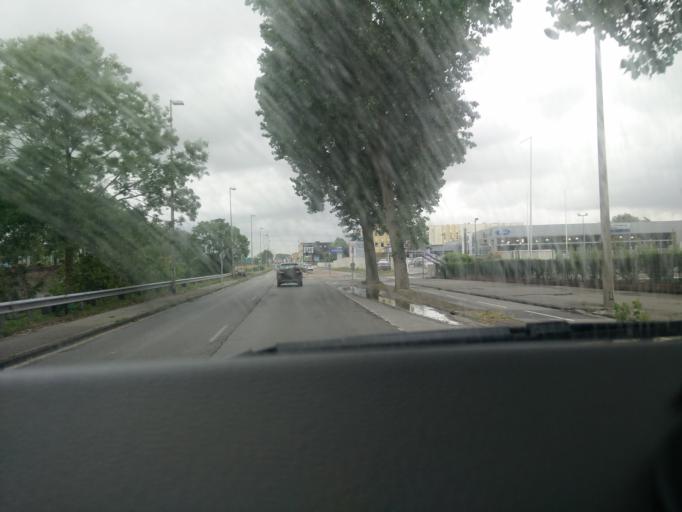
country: FR
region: Nord-Pas-de-Calais
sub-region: Departement du Nord
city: Dunkerque
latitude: 51.0264
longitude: 2.3730
